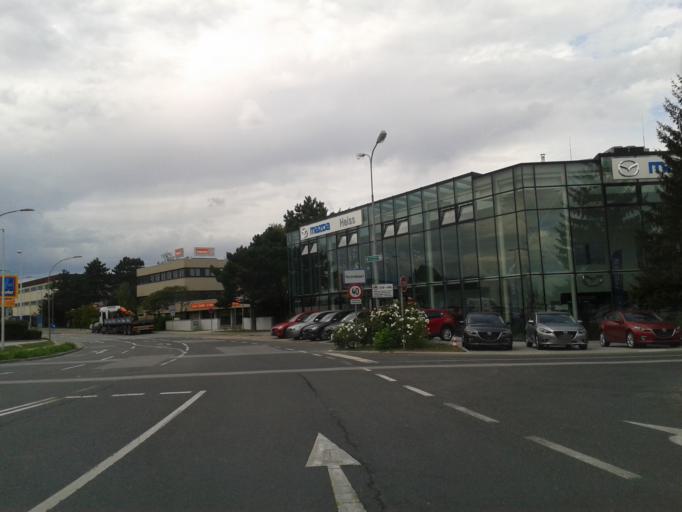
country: AT
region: Lower Austria
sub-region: Politischer Bezirk Modling
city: Brunn am Gebirge
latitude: 48.1236
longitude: 16.2941
